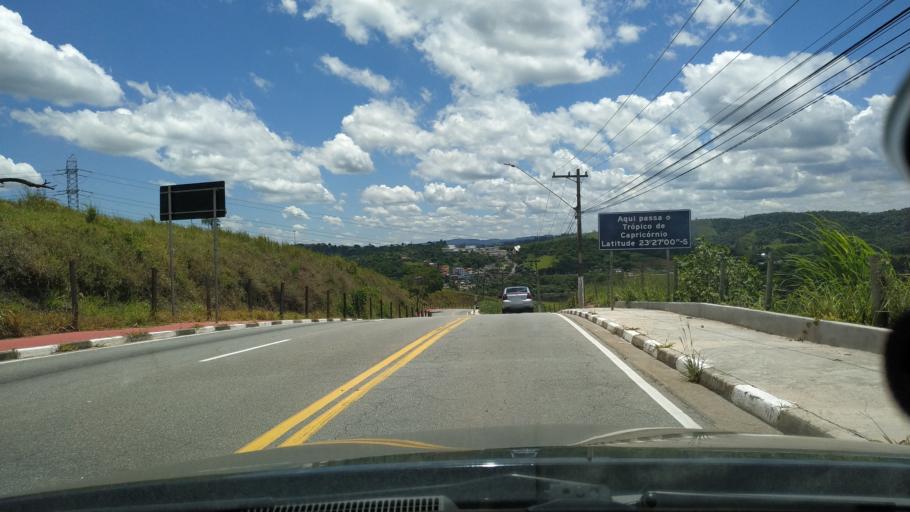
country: BR
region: Sao Paulo
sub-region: Santana De Parnaiba
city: Santana de Parnaiba
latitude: -23.4501
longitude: -46.9052
